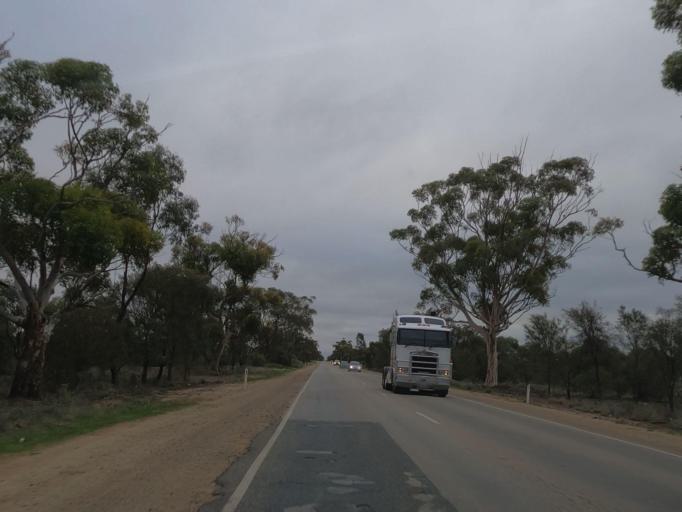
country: AU
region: Victoria
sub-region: Swan Hill
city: Swan Hill
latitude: -35.4102
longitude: 143.5849
